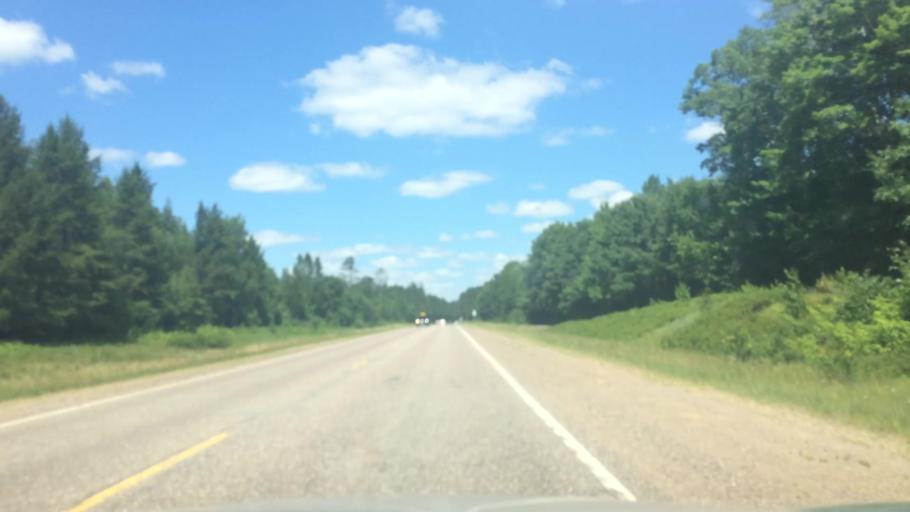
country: US
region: Wisconsin
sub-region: Vilas County
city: Lac du Flambeau
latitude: 46.0786
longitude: -89.6444
